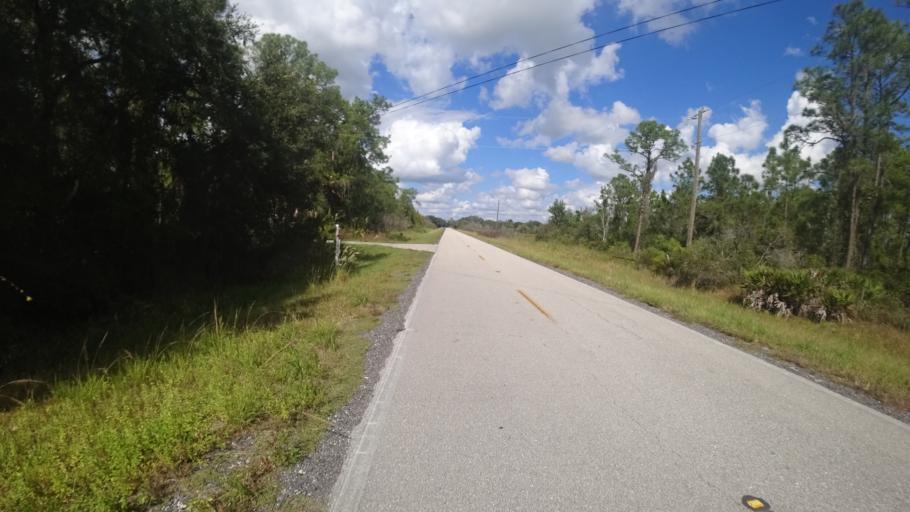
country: US
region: Florida
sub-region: Sarasota County
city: Warm Mineral Springs
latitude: 27.2514
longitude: -82.1219
